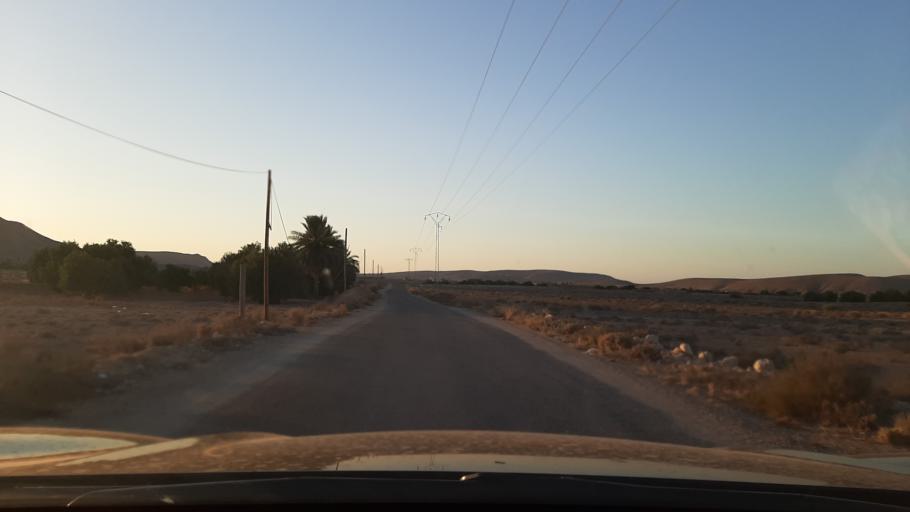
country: TN
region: Qabis
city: Matmata
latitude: 33.5450
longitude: 10.1923
